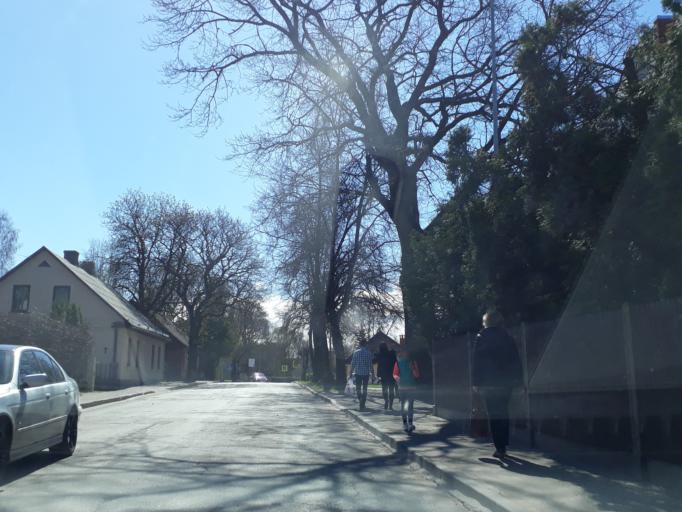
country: LV
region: Dobeles Rajons
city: Dobele
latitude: 56.6176
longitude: 23.2828
